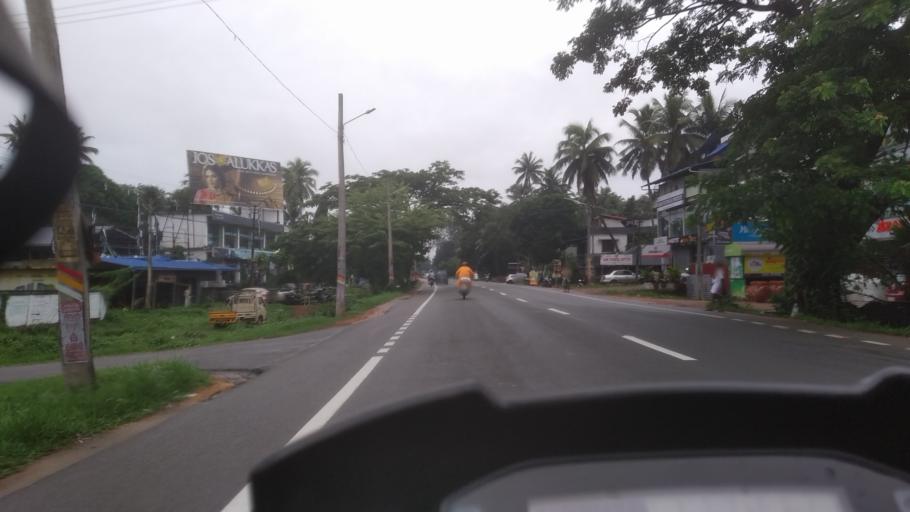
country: IN
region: Kerala
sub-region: Alappuzha
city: Kayankulam
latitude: 9.1832
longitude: 76.4907
